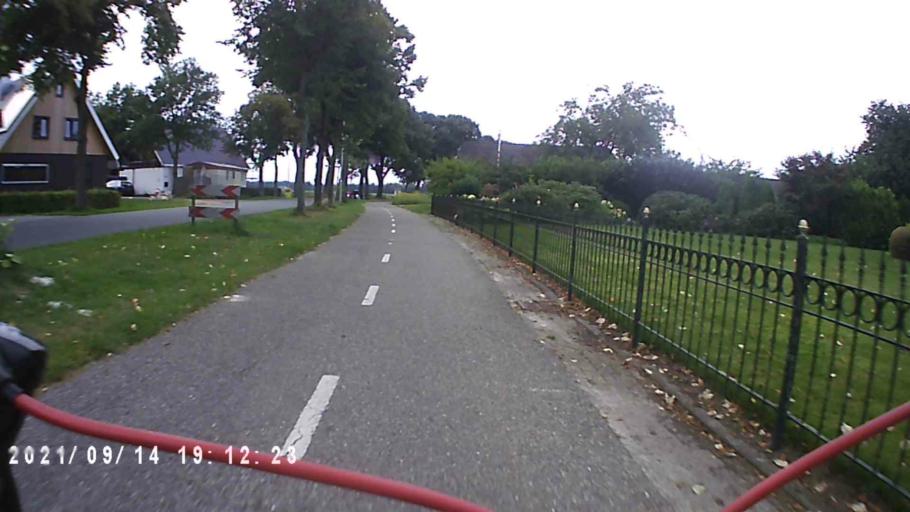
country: NL
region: Drenthe
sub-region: Gemeente Aa en Hunze
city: Anloo
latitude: 53.0632
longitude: 6.7127
